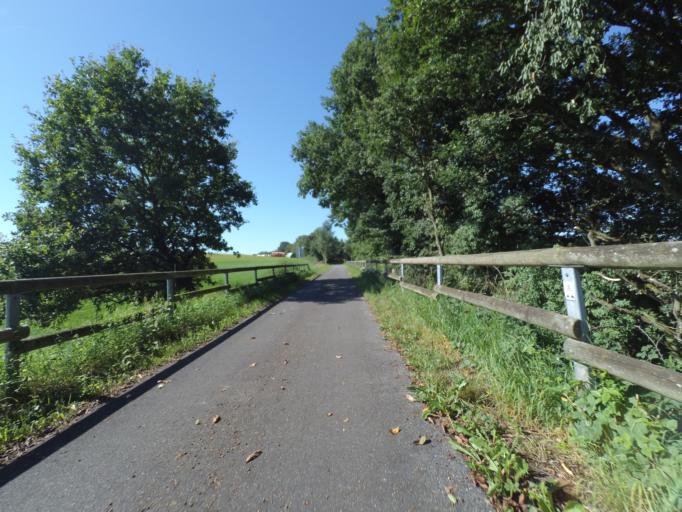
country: DE
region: Rheinland-Pfalz
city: Eckfeld
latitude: 50.1091
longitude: 6.8491
